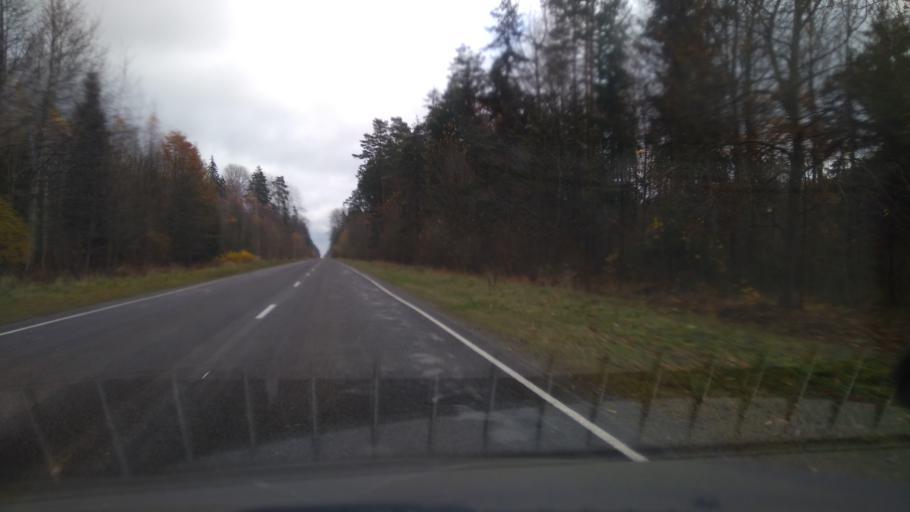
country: BY
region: Minsk
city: Urechcha
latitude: 53.2080
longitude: 27.9265
